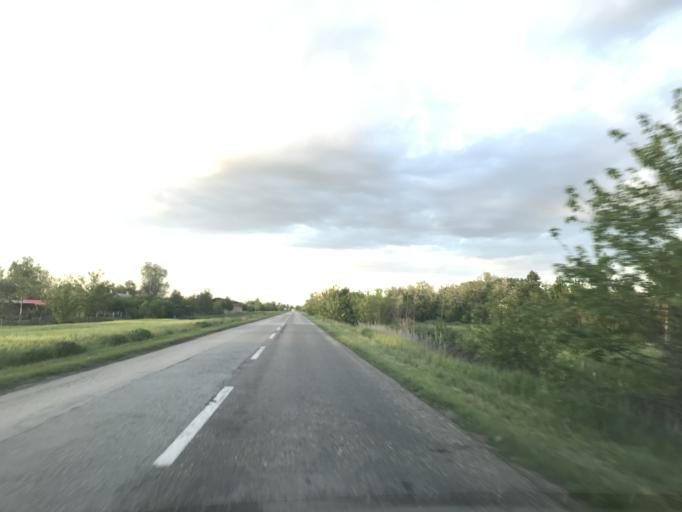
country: RS
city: Banatsko Karadordevo
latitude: 45.5854
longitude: 20.5521
